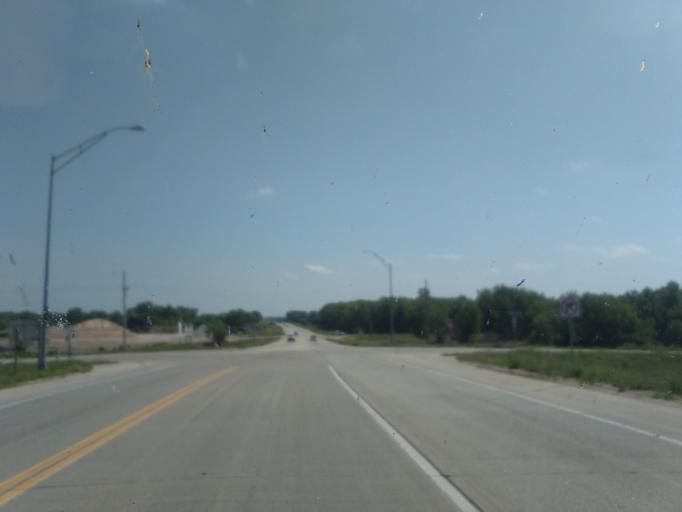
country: US
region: Nebraska
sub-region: Phelps County
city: Holdrege
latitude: 40.6891
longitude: -99.3799
